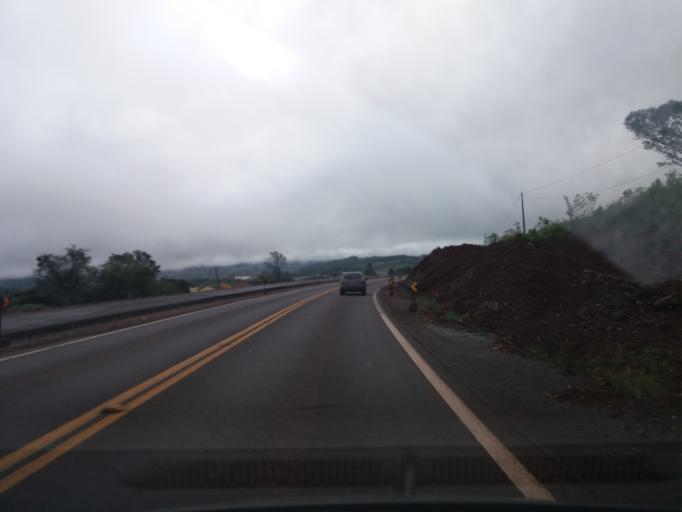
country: BR
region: Parana
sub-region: Cascavel
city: Cascavel
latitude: -25.2374
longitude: -53.5899
